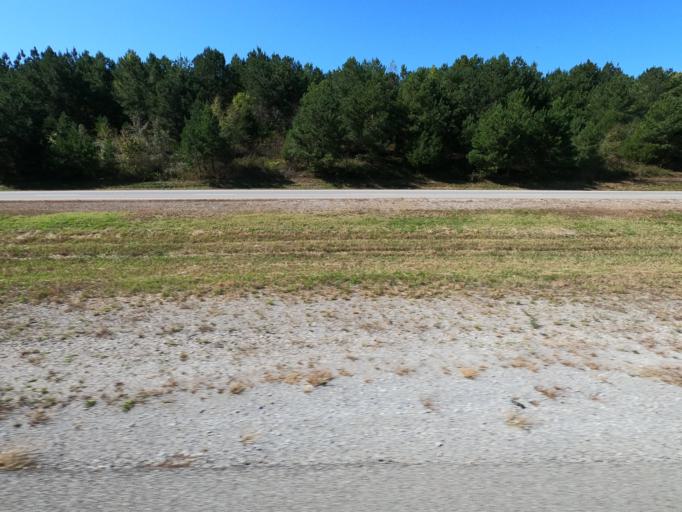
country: US
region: Tennessee
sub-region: Williamson County
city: Fairview
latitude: 35.8778
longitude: -87.0975
